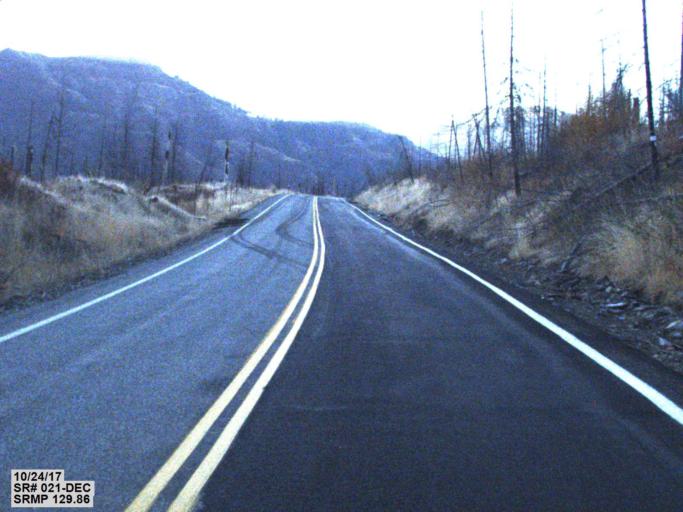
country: US
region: Washington
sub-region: Ferry County
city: Republic
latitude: 48.2588
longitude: -118.6924
